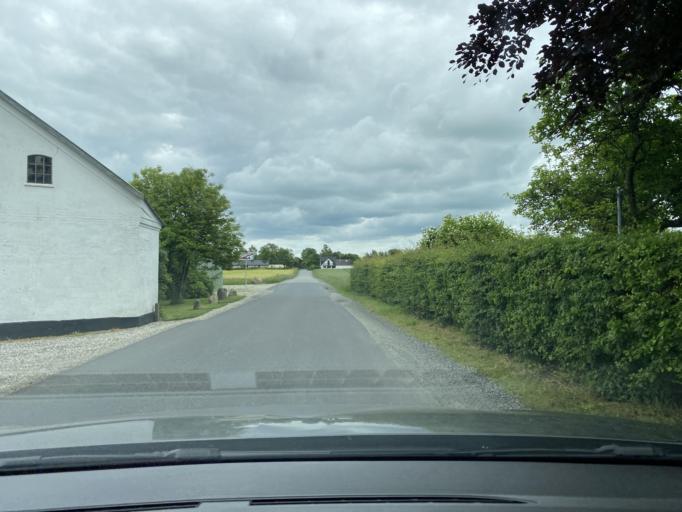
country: DK
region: South Denmark
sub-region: Vejle Kommune
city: Jelling
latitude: 55.6703
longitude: 9.4425
